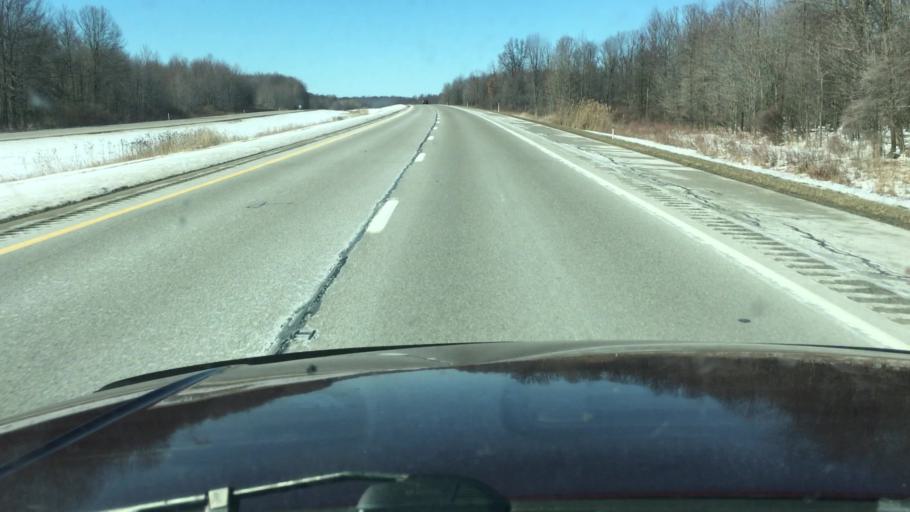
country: US
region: Pennsylvania
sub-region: Crawford County
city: Cochranton
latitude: 41.4971
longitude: -80.1672
